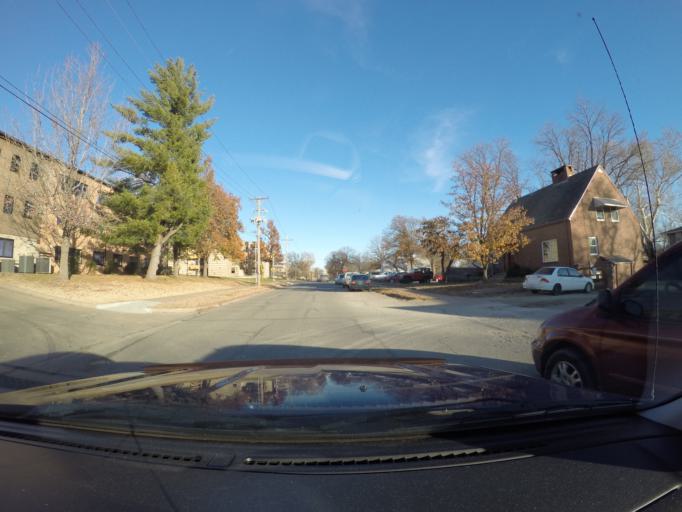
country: US
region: Kansas
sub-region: Riley County
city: Manhattan
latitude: 39.1896
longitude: -96.5897
